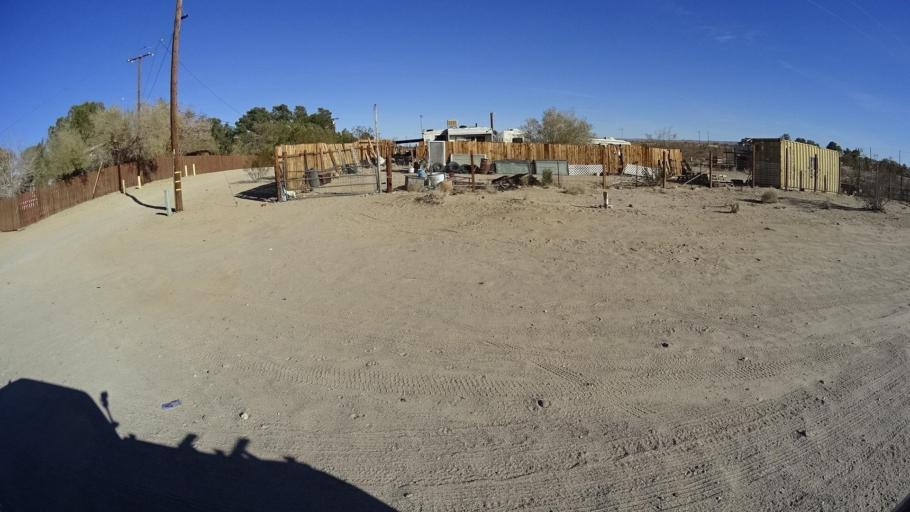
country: US
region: California
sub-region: Kern County
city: China Lake Acres
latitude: 35.6388
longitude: -117.7586
